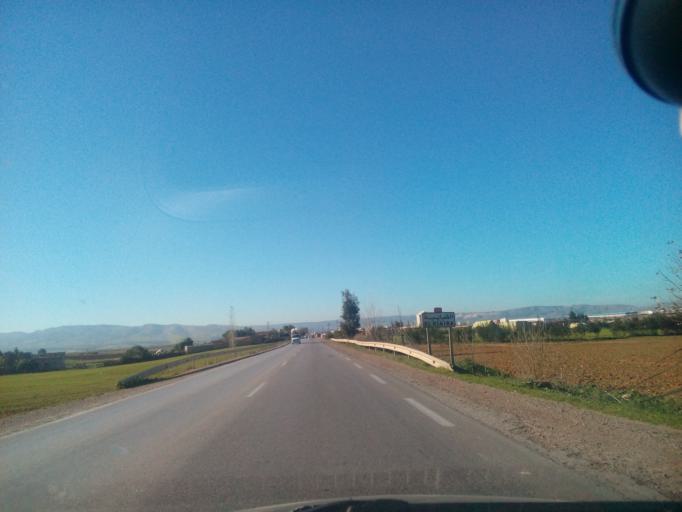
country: DZ
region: Relizane
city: Relizane
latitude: 35.8968
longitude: 0.5944
